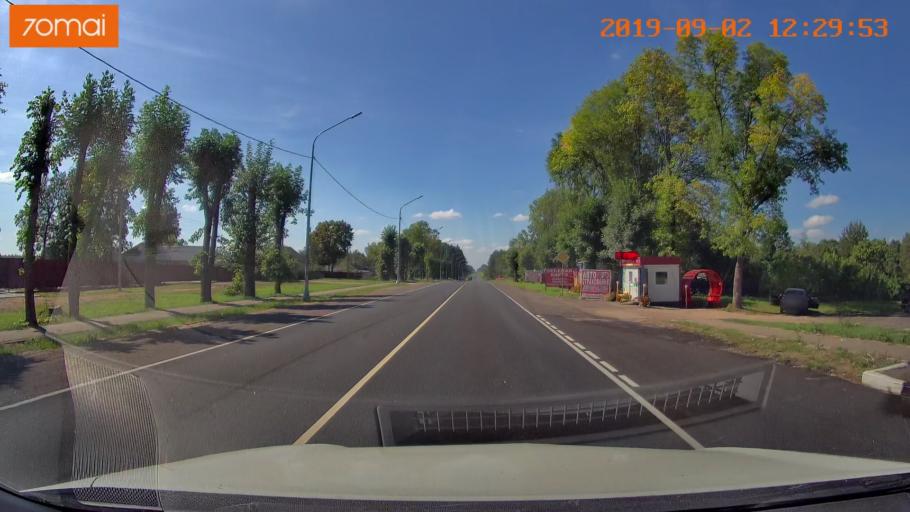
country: RU
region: Smolensk
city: Shumyachi
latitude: 53.8354
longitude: 32.4853
